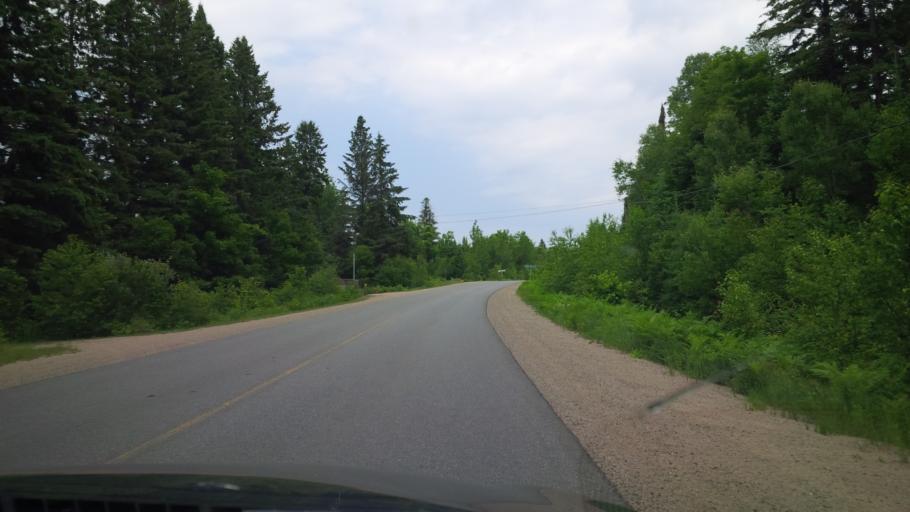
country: CA
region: Ontario
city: Huntsville
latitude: 45.6073
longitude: -79.1762
